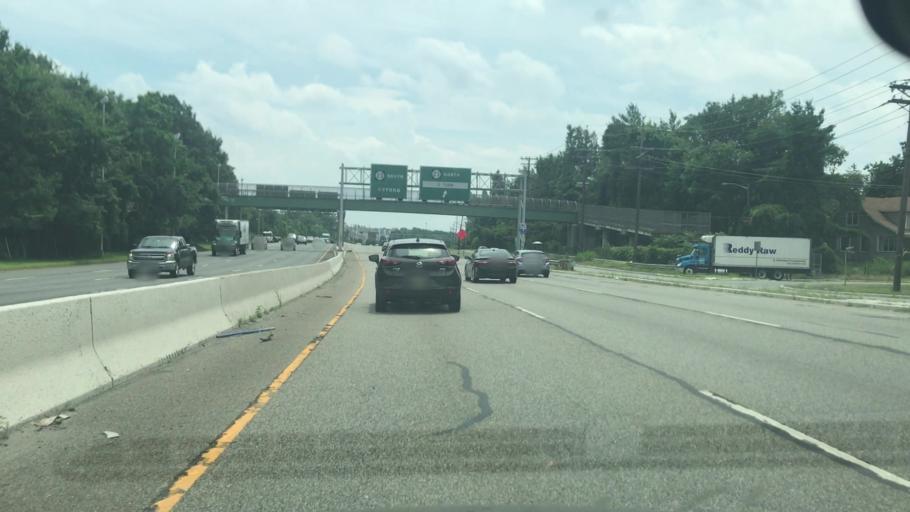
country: US
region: New Jersey
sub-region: Passaic County
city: Wayne
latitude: 40.9099
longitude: -74.2628
